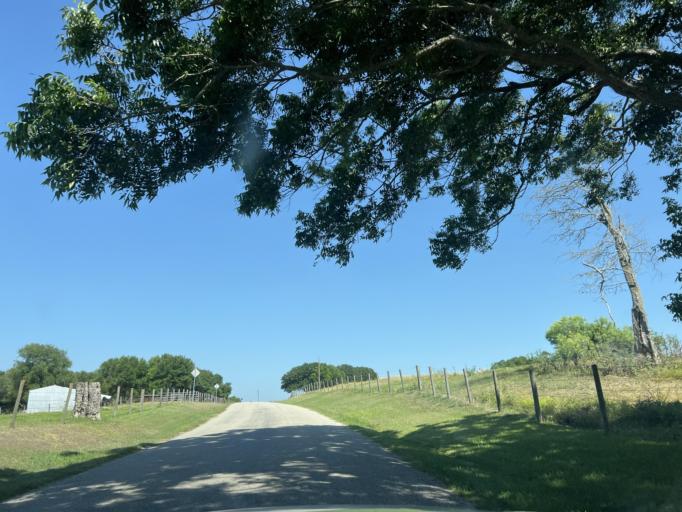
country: US
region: Texas
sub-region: Washington County
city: Brenham
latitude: 30.1714
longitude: -96.3381
